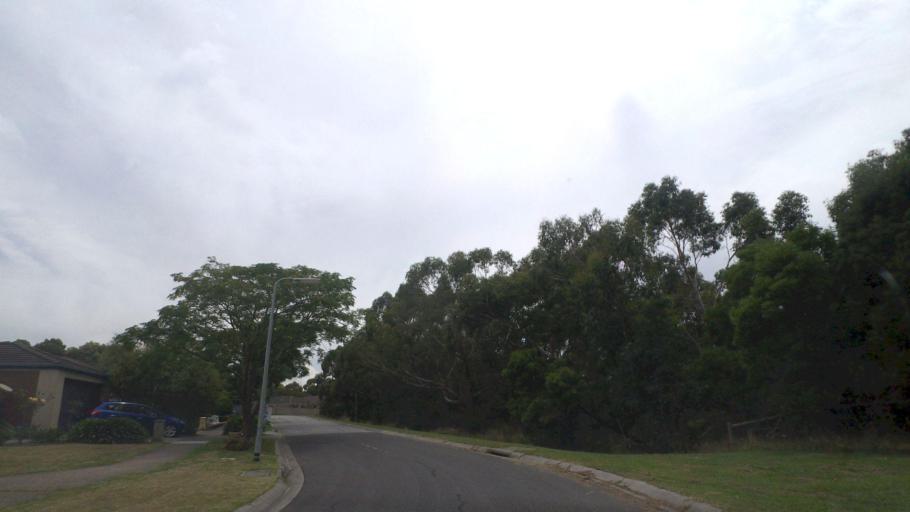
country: AU
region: Victoria
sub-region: Yarra Ranges
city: Lilydale
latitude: -37.7699
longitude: 145.3508
